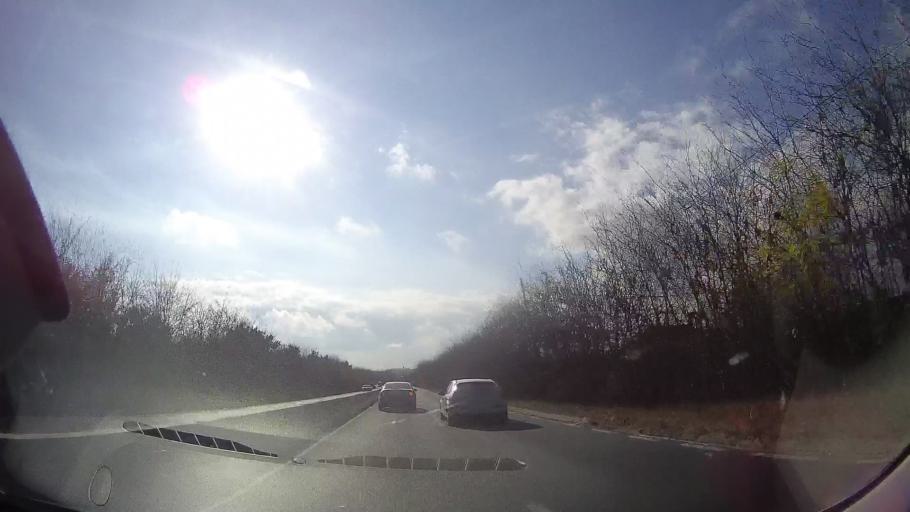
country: RO
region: Constanta
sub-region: Comuna Agigea
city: Agigea
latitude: 44.1232
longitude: 28.6134
